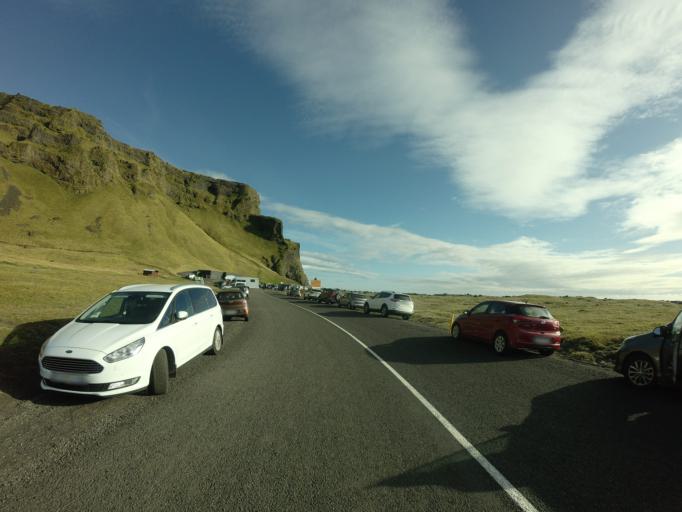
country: IS
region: South
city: Vestmannaeyjar
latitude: 63.4049
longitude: -19.0473
